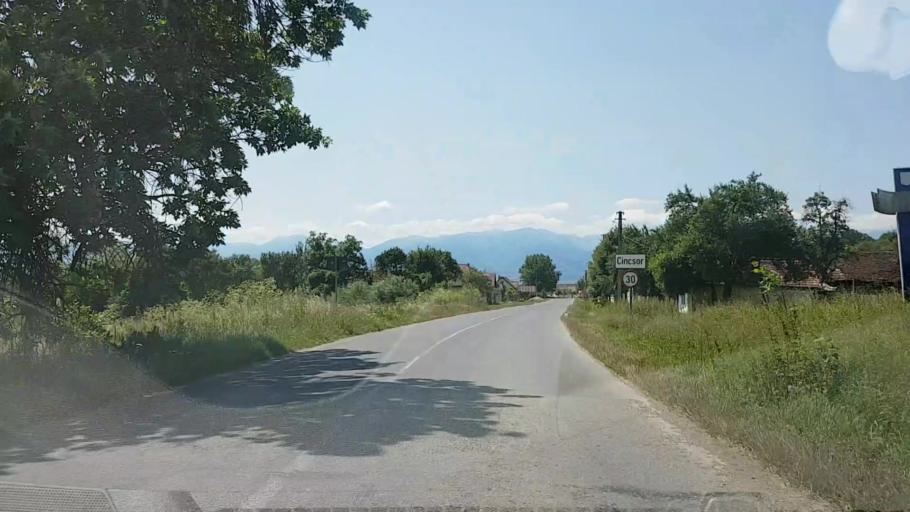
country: RO
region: Brasov
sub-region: Comuna Voila
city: Voila
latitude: 45.8455
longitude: 24.8332
